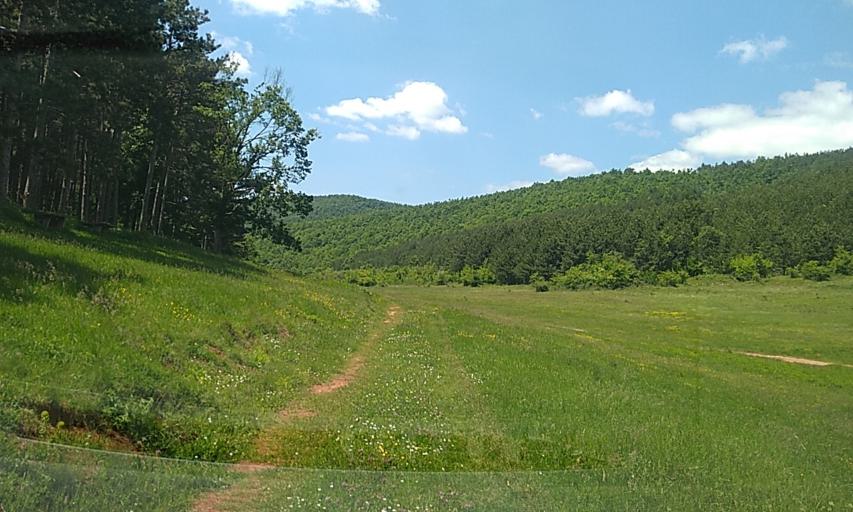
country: RS
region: Central Serbia
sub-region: Nisavski Okrug
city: Niska Banja
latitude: 43.3758
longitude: 21.9991
